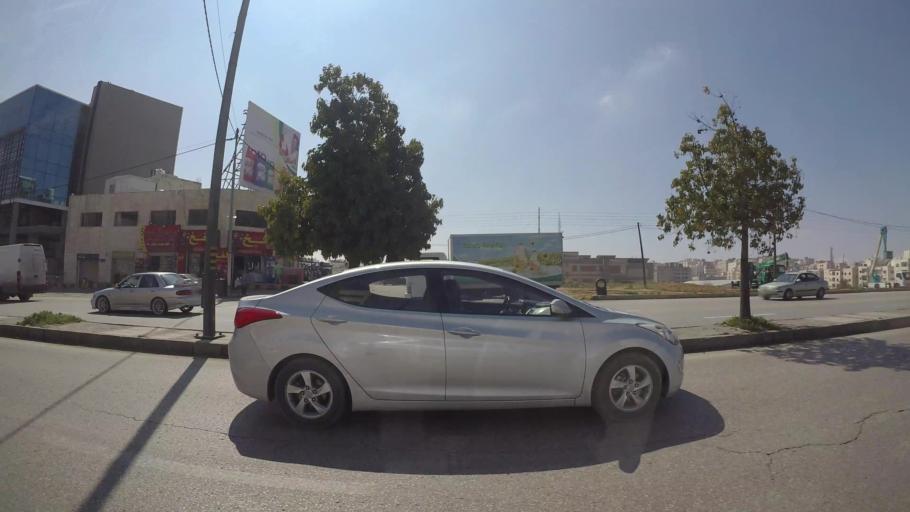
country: JO
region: Amman
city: Al Bunayyat ash Shamaliyah
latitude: 31.9184
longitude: 35.8986
